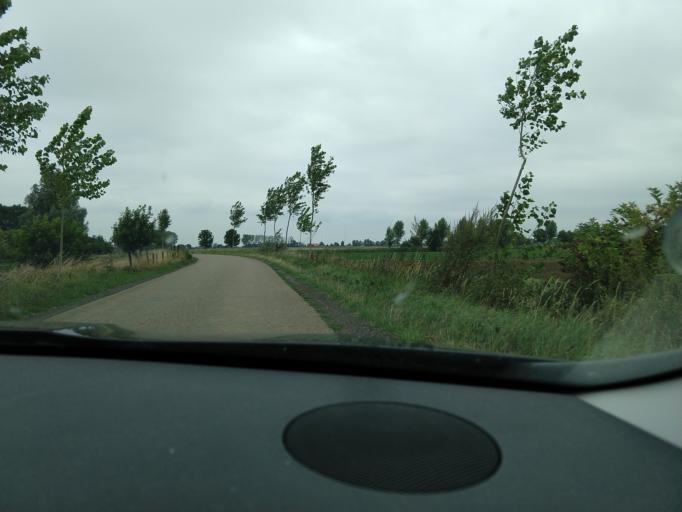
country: NL
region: Zeeland
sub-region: Gemeente Hulst
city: Hulst
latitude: 51.3303
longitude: 4.0632
